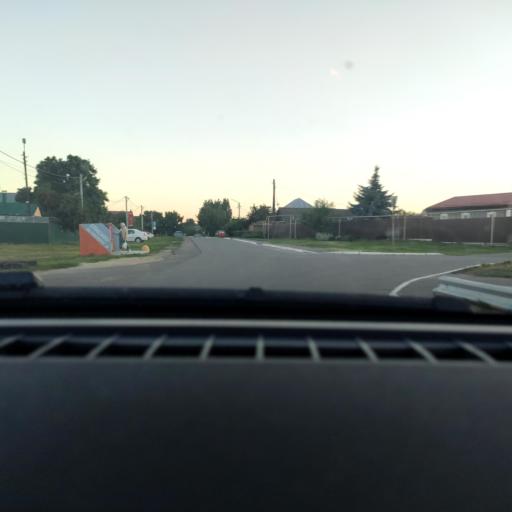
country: RU
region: Voronezj
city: Novaya Usman'
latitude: 51.6597
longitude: 39.3405
